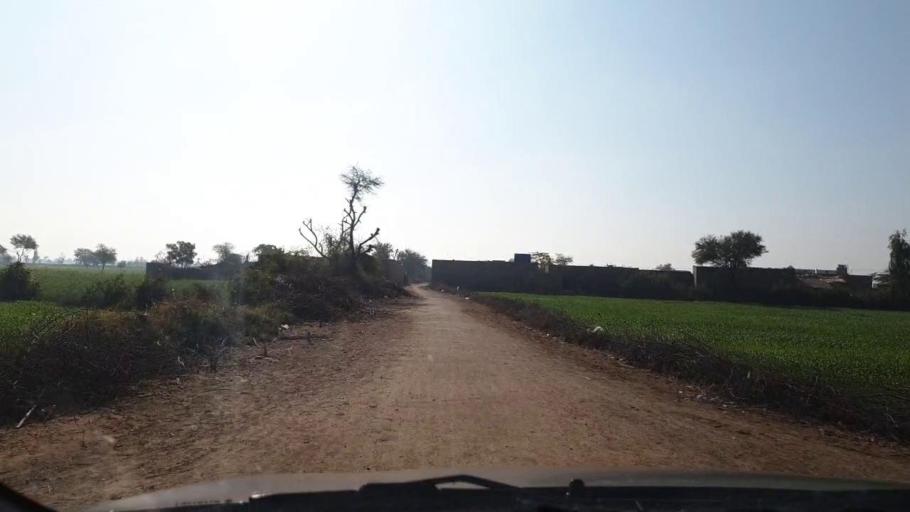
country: PK
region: Sindh
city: Sinjhoro
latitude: 26.0003
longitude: 68.7782
